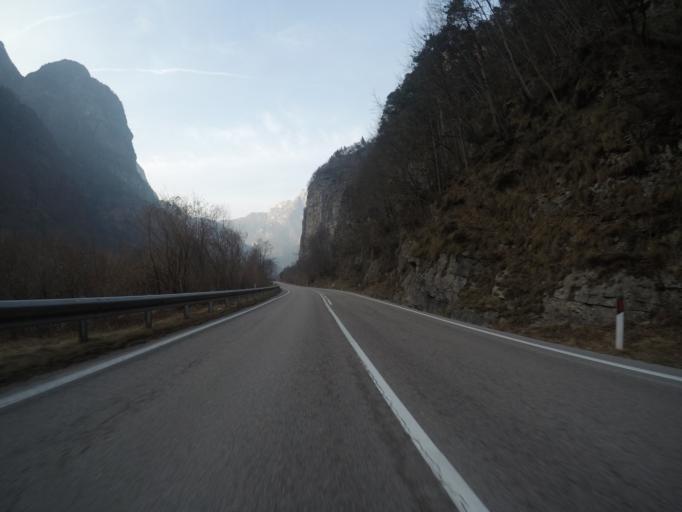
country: IT
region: Veneto
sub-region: Provincia di Belluno
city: La Valle Agordina
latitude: 46.2279
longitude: 12.1160
